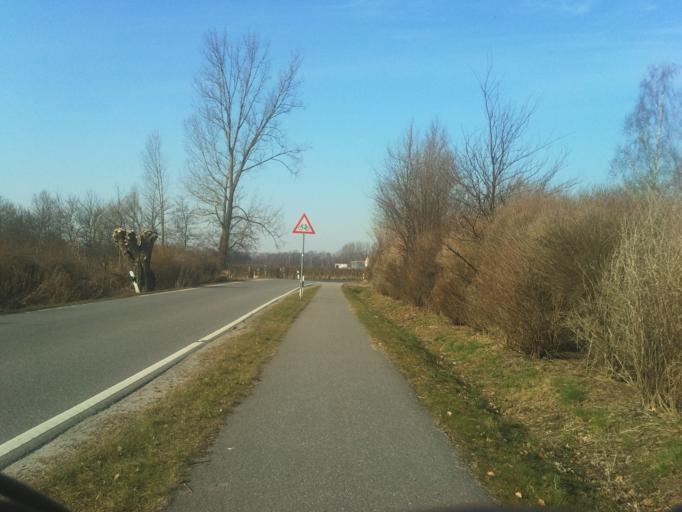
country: DE
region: Mecklenburg-Vorpommern
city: Lambrechtshagen
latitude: 54.1192
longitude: 12.0331
